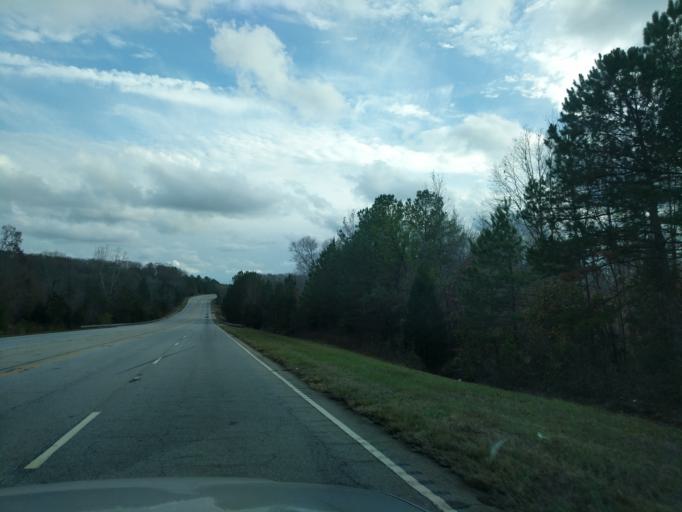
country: US
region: South Carolina
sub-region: Greenwood County
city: Ware Shoals
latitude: 34.4114
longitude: -82.2281
